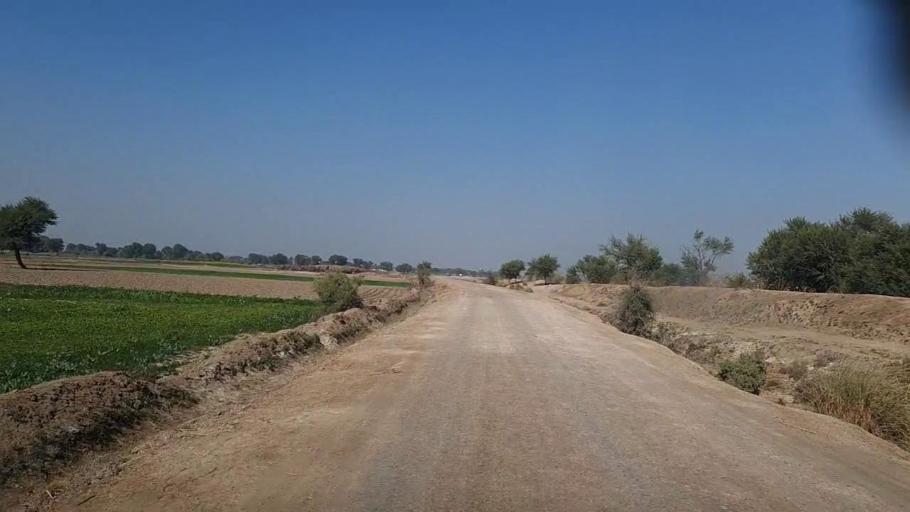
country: PK
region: Sindh
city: Khairpur
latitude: 27.9866
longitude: 69.8487
